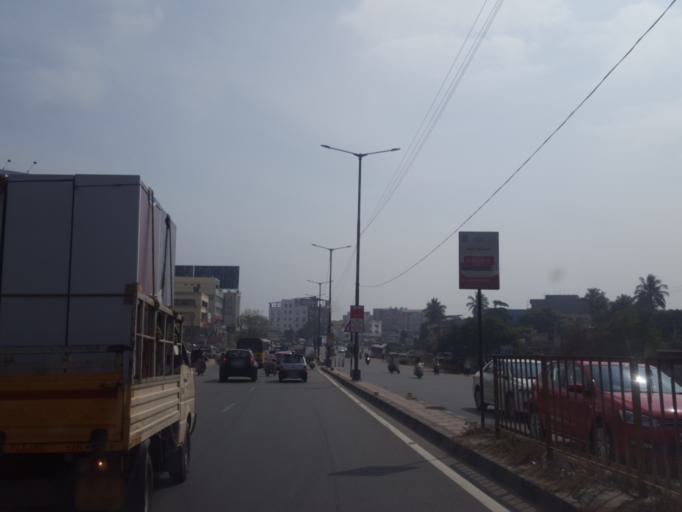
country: IN
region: Telangana
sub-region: Medak
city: Serilingampalle
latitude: 17.5040
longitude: 78.3094
